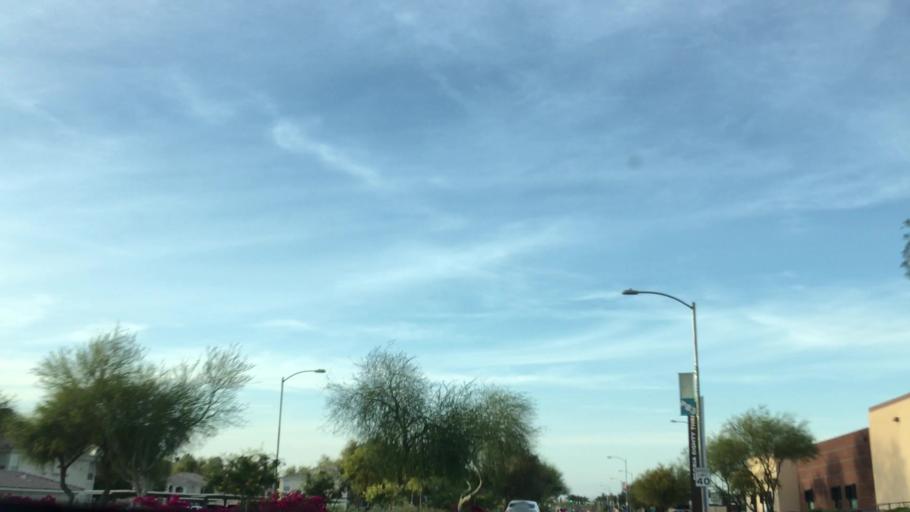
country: US
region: Arizona
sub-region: Maricopa County
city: Sun City
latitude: 33.6249
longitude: -112.2374
